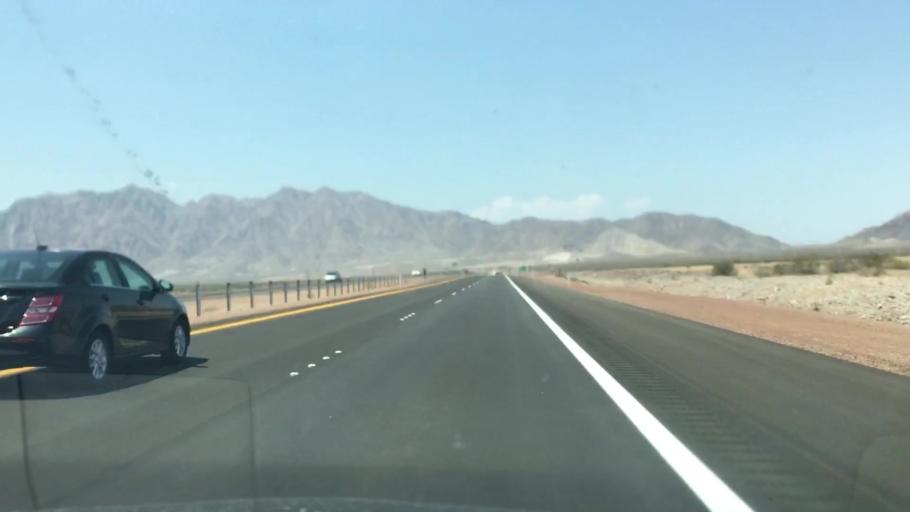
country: US
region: Nevada
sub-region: Clark County
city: Boulder City
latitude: 35.9396
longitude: -114.8742
